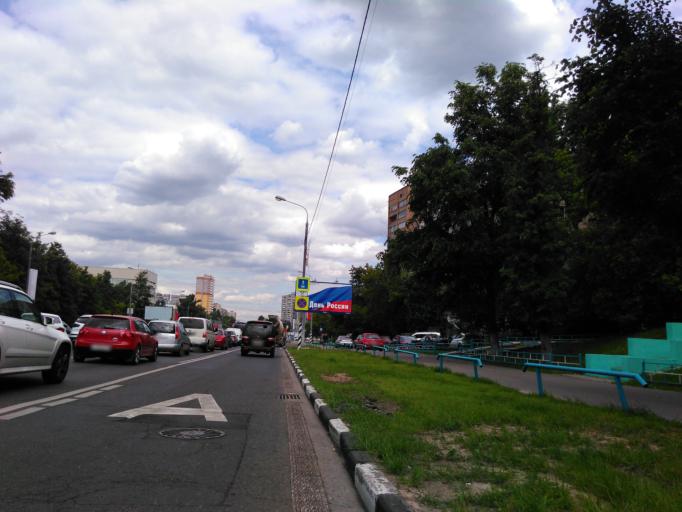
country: RU
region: Moscow
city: Kotlovka
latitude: 55.6776
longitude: 37.5939
